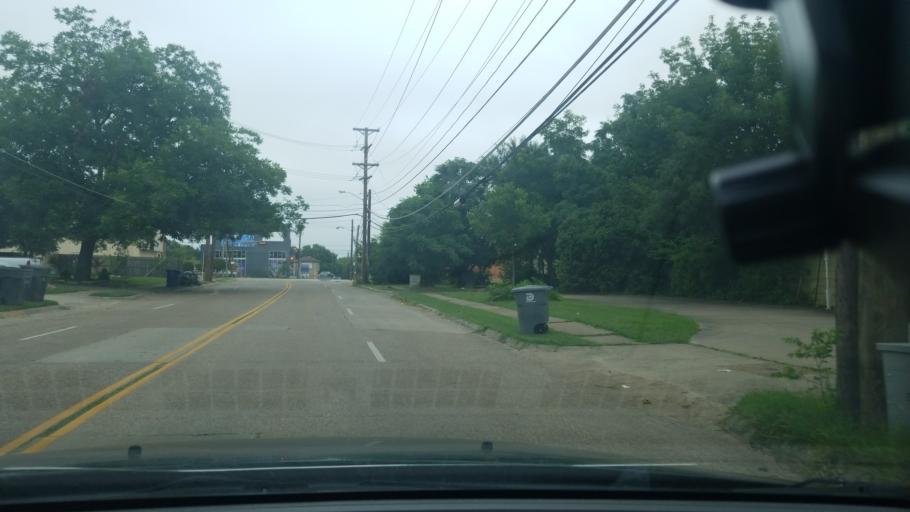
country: US
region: Texas
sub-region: Dallas County
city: Balch Springs
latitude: 32.7580
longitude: -96.6843
